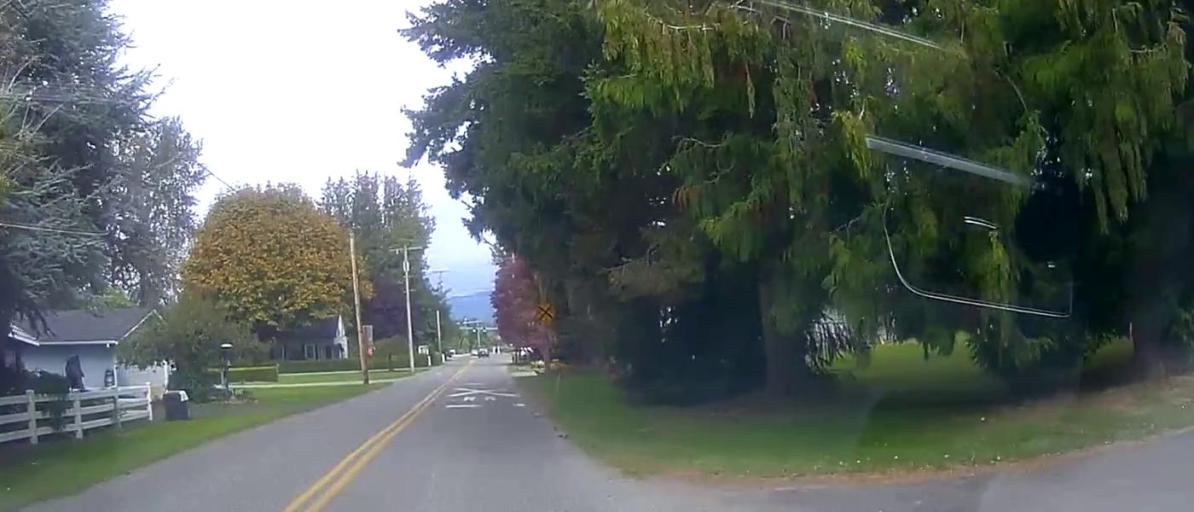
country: US
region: Washington
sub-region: Skagit County
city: Sedro-Woolley
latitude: 48.4989
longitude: -122.2583
